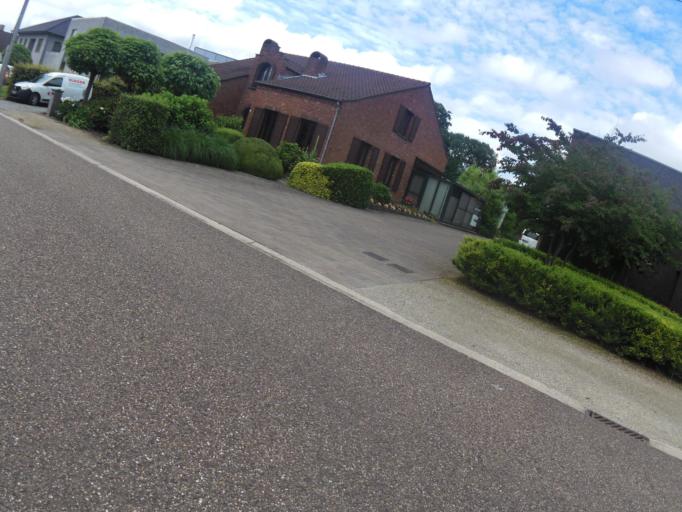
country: BE
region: Flanders
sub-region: Provincie Antwerpen
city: Kasterlee
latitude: 51.2078
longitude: 4.9872
